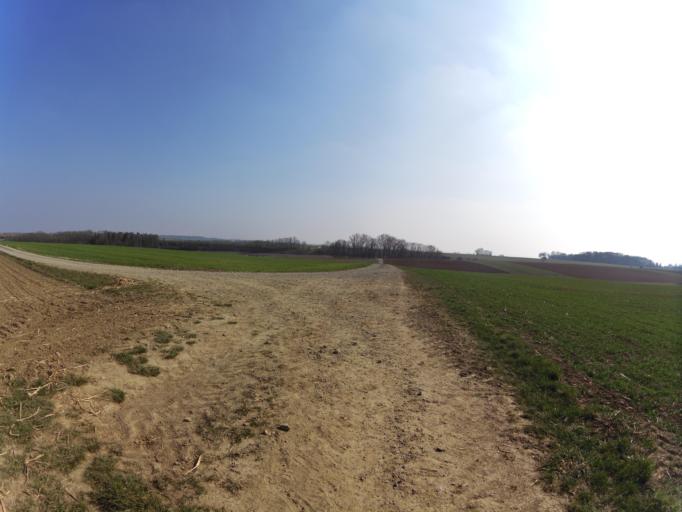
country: DE
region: Bavaria
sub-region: Regierungsbezirk Unterfranken
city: Gaukonigshofen
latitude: 49.6688
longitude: 9.9862
